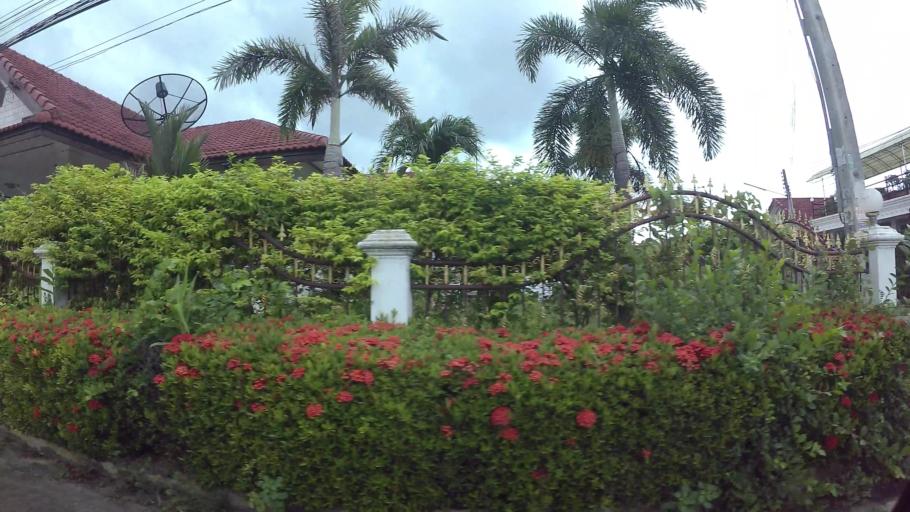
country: TH
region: Chon Buri
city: Sattahip
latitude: 12.7271
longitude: 100.8985
